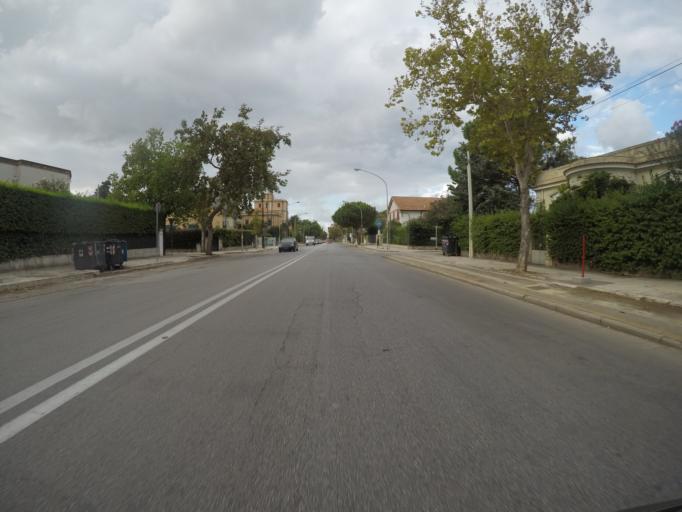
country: IT
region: Sicily
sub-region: Palermo
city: Palermo
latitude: 38.1923
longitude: 13.3325
